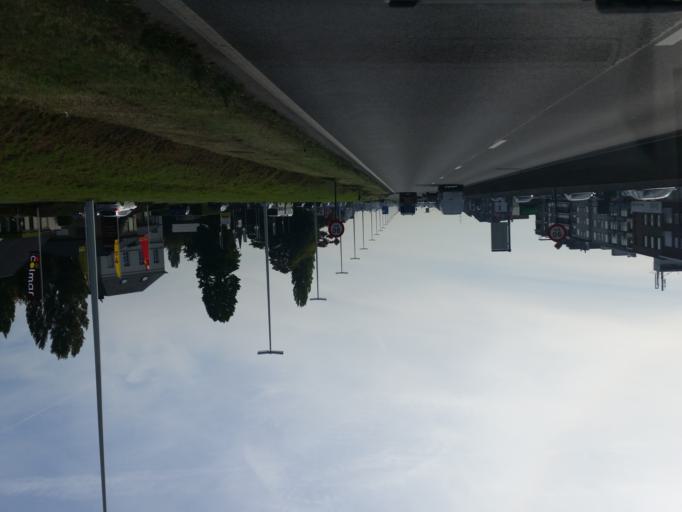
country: BE
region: Flanders
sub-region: Provincie Antwerpen
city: Aartselaar
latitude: 51.1422
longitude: 4.3792
